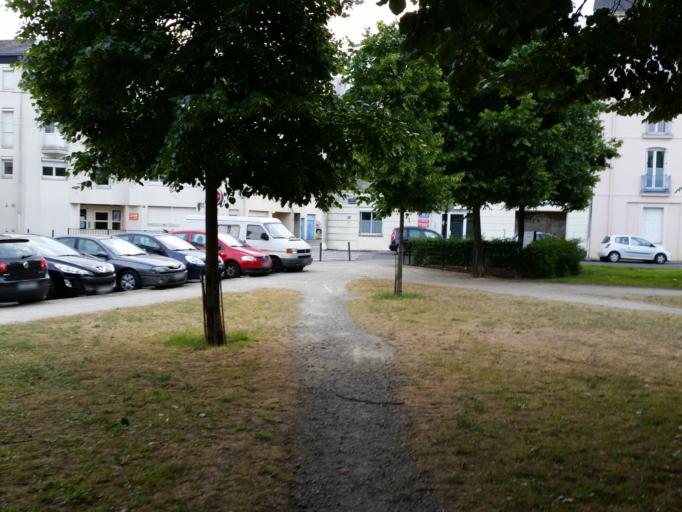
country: FR
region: Pays de la Loire
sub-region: Departement de la Loire-Atlantique
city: Nantes
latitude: 47.2039
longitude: -1.5482
